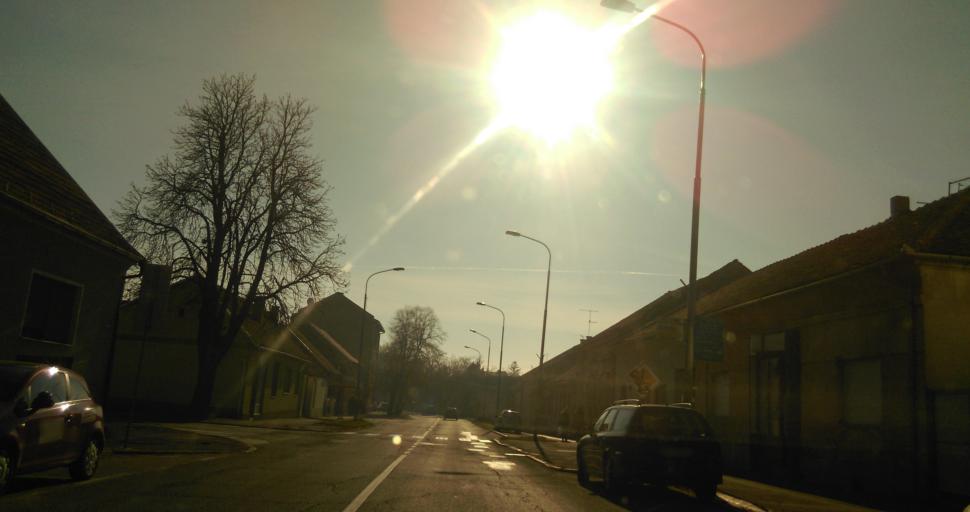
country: RS
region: Autonomna Pokrajina Vojvodina
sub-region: Sremski Okrug
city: Ruma
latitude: 45.0035
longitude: 19.8222
